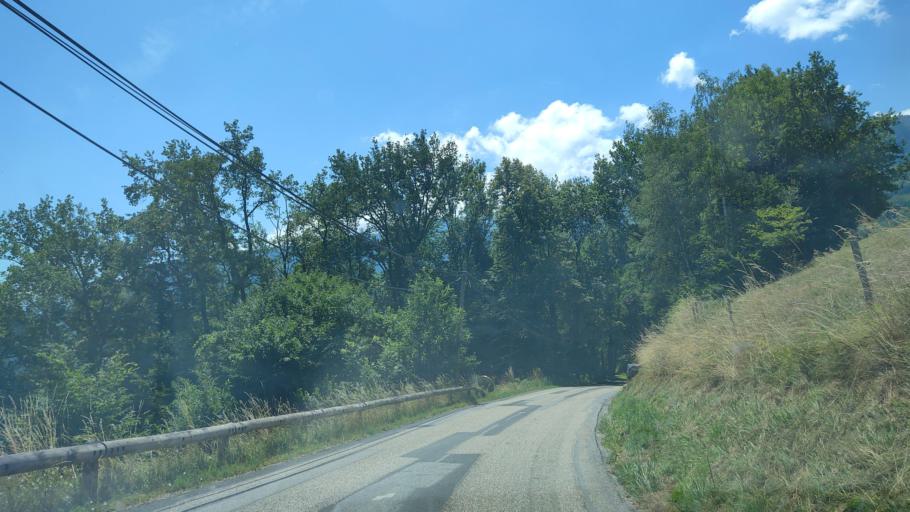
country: FR
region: Rhone-Alpes
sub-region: Departement de la Savoie
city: Aiton
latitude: 45.4950
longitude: 6.2822
